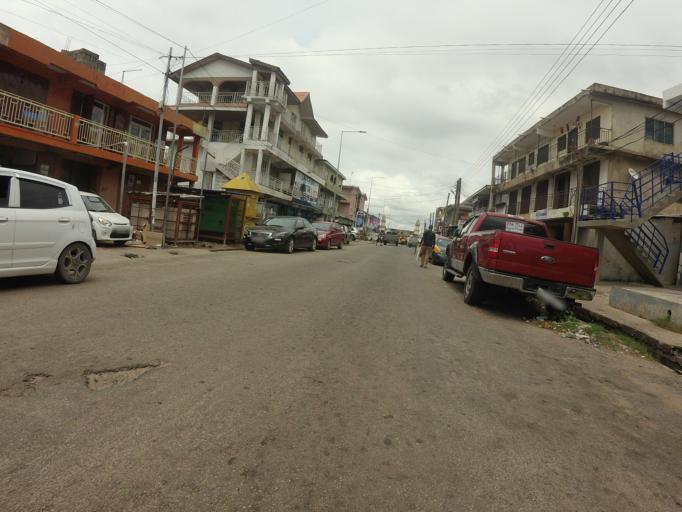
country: GH
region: Greater Accra
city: Accra
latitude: 5.5815
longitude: -0.2074
